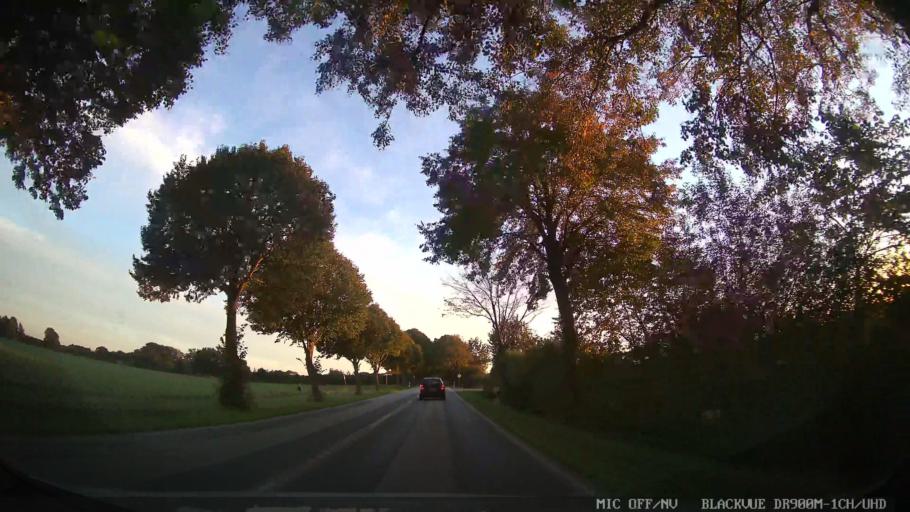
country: DE
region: Schleswig-Holstein
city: Susel
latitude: 54.0545
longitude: 10.6823
